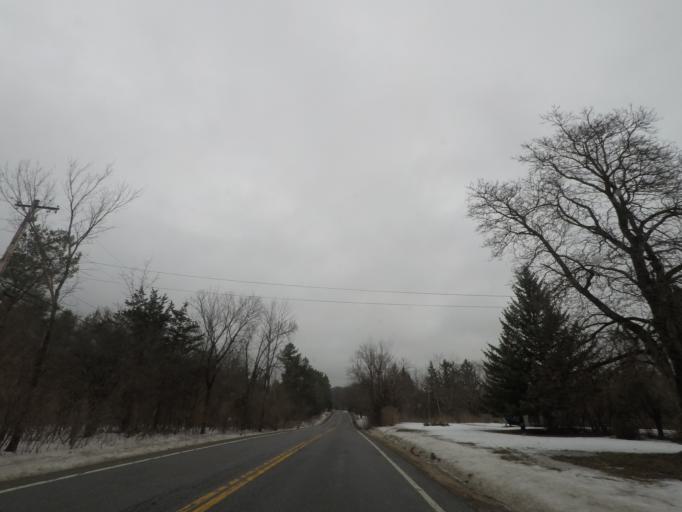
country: US
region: New York
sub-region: Albany County
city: Altamont
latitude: 42.6680
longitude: -74.0052
